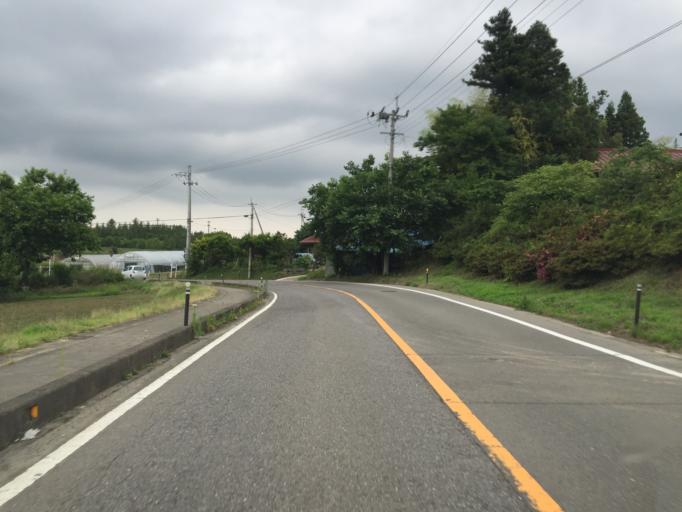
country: JP
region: Fukushima
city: Nihommatsu
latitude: 37.6100
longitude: 140.4813
